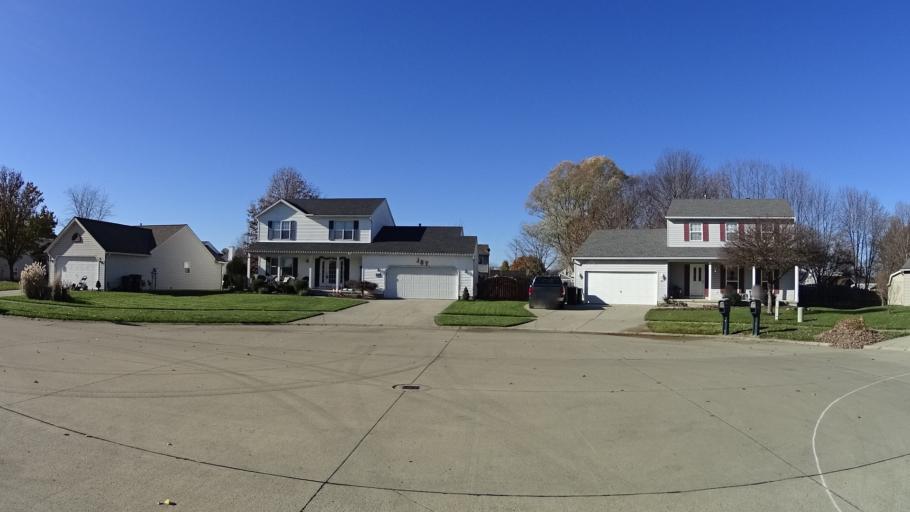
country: US
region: Ohio
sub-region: Lorain County
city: Elyria
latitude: 41.3512
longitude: -82.0750
